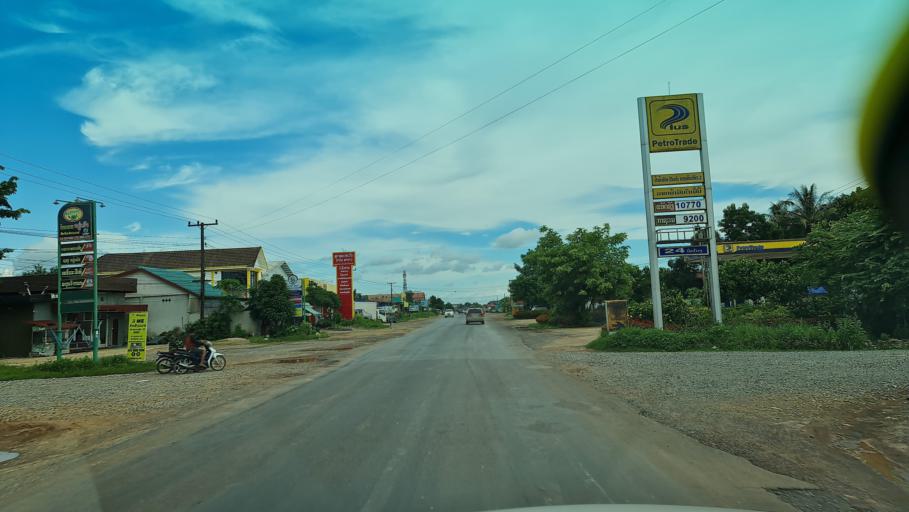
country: LA
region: Bolikhamxai
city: Ban Nahin
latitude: 18.1062
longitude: 104.2815
